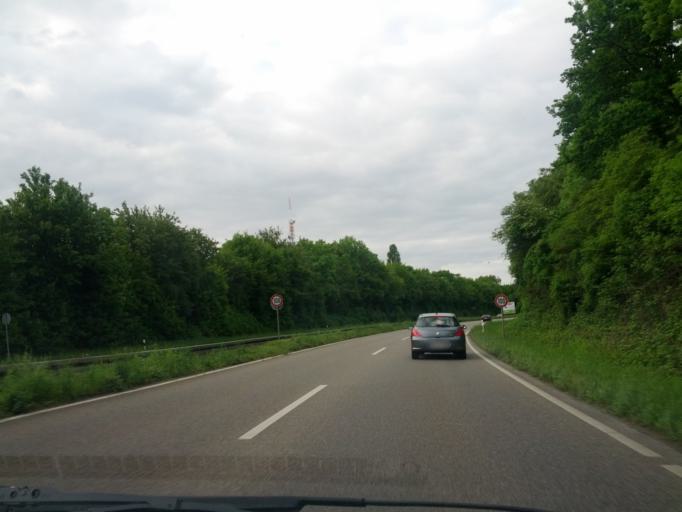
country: DE
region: Baden-Wuerttemberg
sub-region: Freiburg Region
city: Gundelfingen
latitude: 48.0241
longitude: 7.8566
